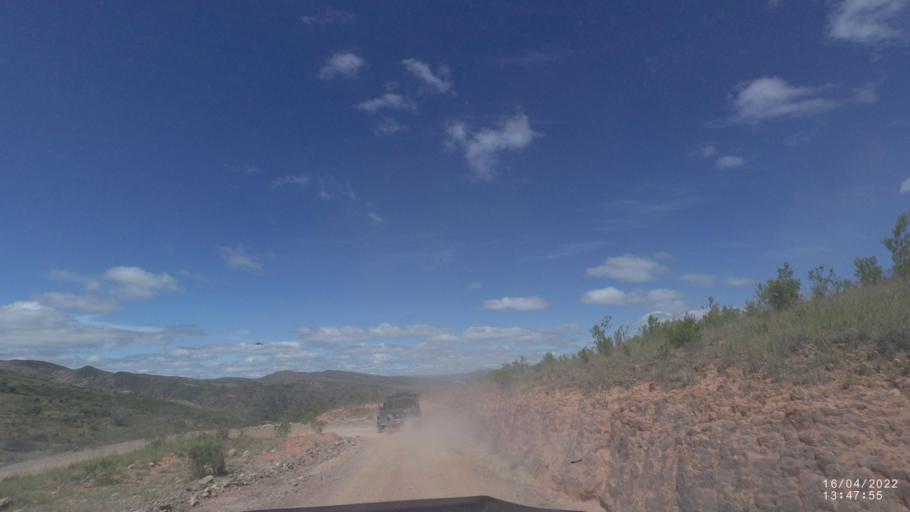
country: BO
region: Cochabamba
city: Mizque
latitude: -18.0108
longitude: -65.5806
